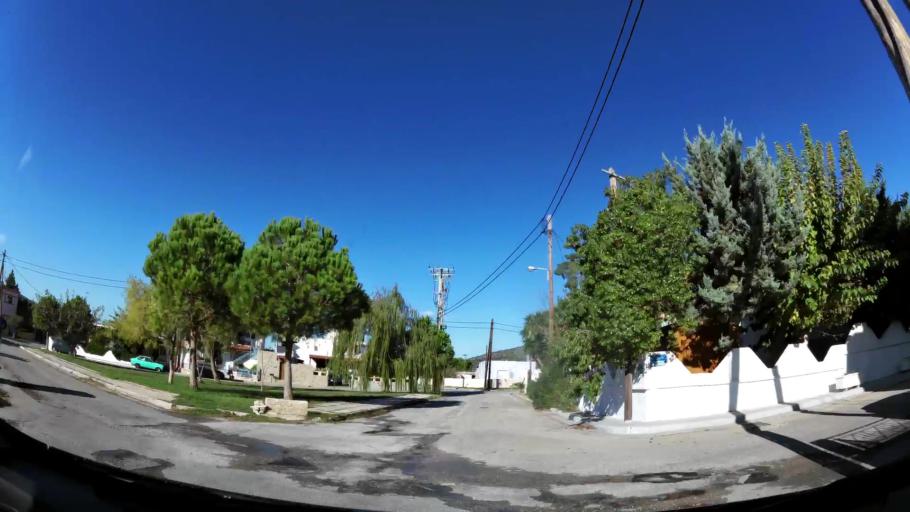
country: GR
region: Attica
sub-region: Nomarchia Anatolikis Attikis
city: Kalyvia Thorikou
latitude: 37.8367
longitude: 23.9249
